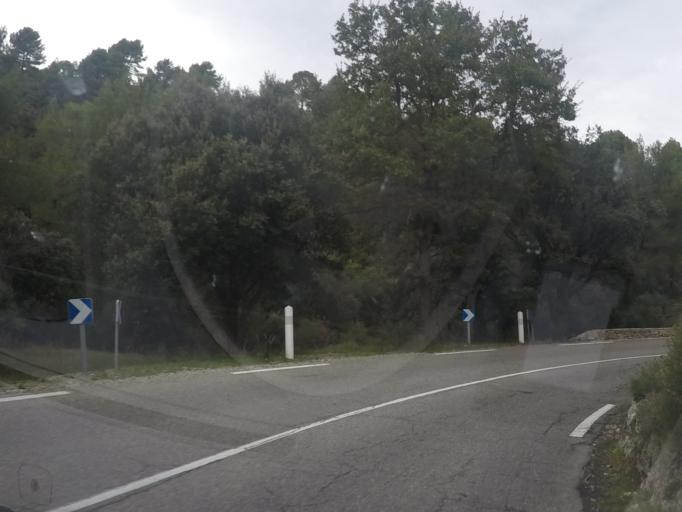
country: FR
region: Provence-Alpes-Cote d'Azur
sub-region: Departement du Vaucluse
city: Lourmarin
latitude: 43.7846
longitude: 5.3462
